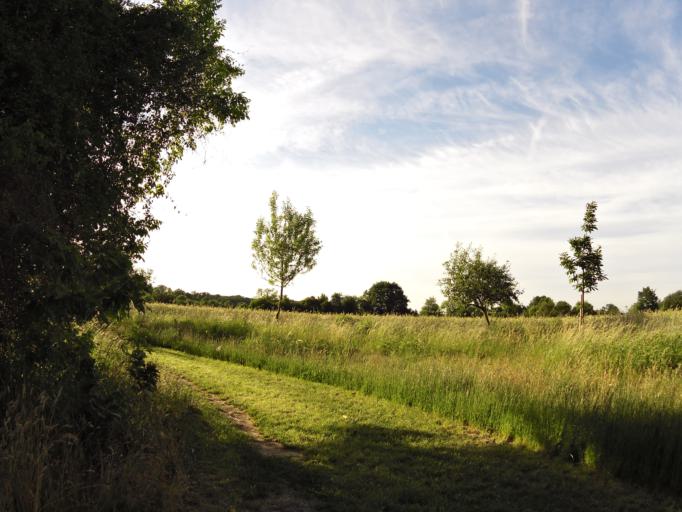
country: DE
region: Hesse
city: Morfelden-Walldorf
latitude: 49.9823
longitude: 8.5598
